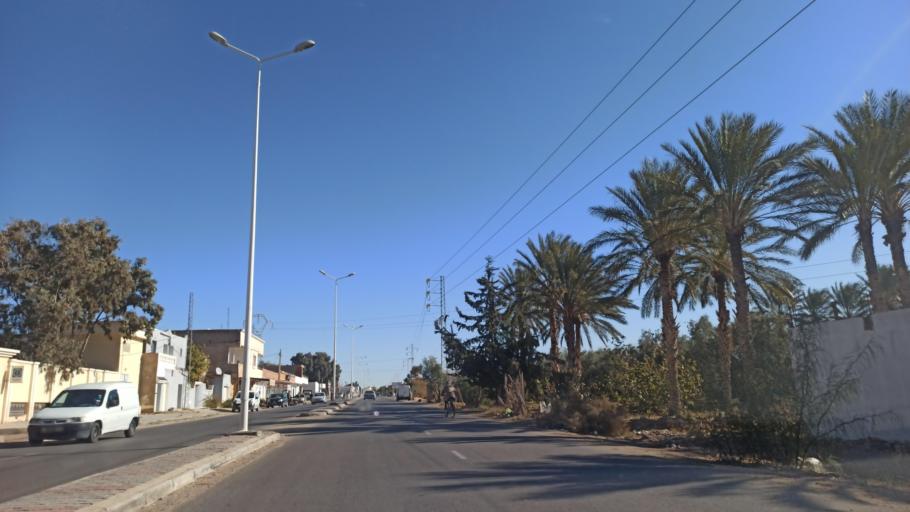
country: TN
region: Gafsa
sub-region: Gafsa Municipality
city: Gafsa
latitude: 34.4231
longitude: 8.7516
